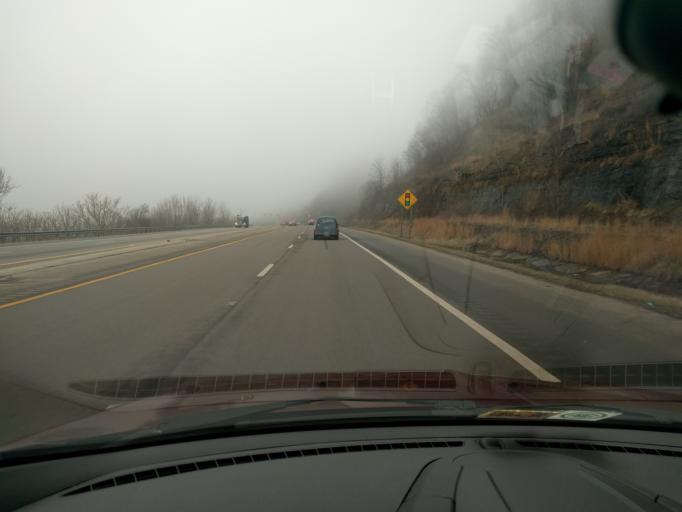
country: US
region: West Virginia
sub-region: Kanawha County
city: Chesapeake
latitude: 38.2093
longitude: -81.5076
